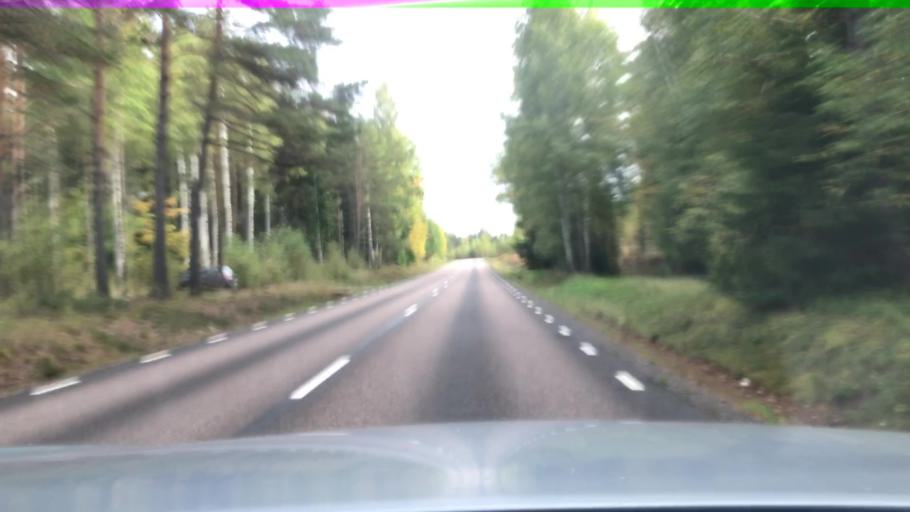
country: SE
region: Vaermland
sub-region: Forshaga Kommun
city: Forshaga
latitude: 59.5061
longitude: 13.4150
